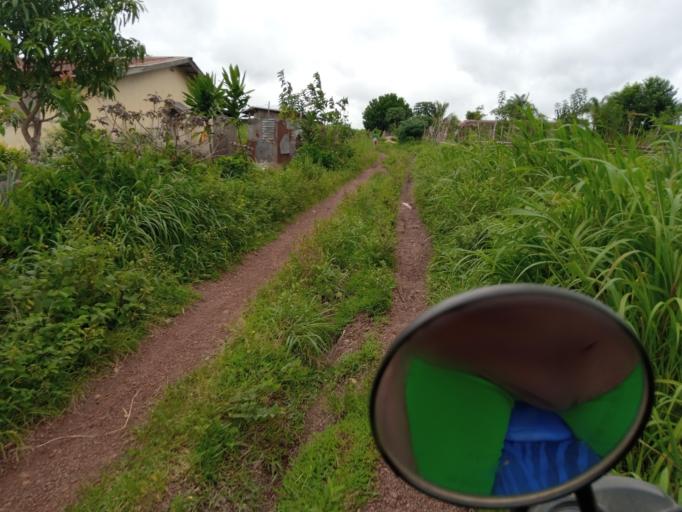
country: SL
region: Southern Province
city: Largo
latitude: 8.1937
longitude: -12.0555
